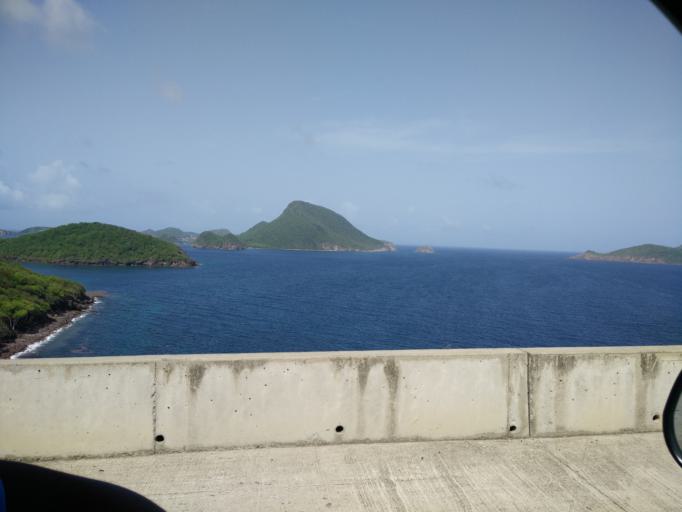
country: GP
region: Guadeloupe
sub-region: Guadeloupe
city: Terre-de-Bas
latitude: 15.8461
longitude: -61.6275
